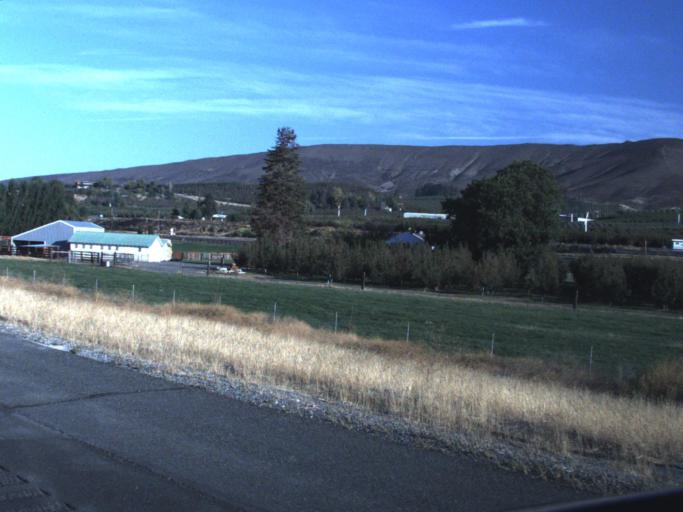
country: US
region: Washington
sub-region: Yakima County
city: Wapato
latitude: 46.4862
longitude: -120.4140
